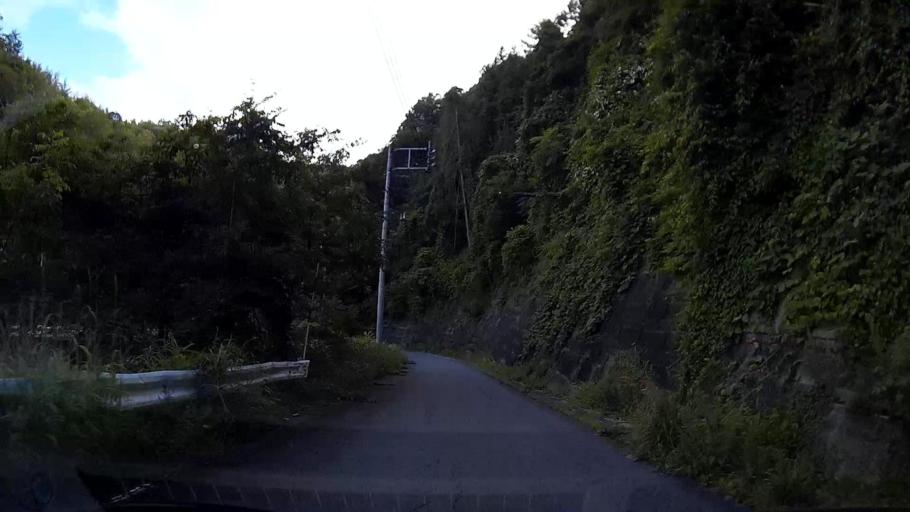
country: JP
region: Gunma
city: Nakanojomachi
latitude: 36.6271
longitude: 138.6290
